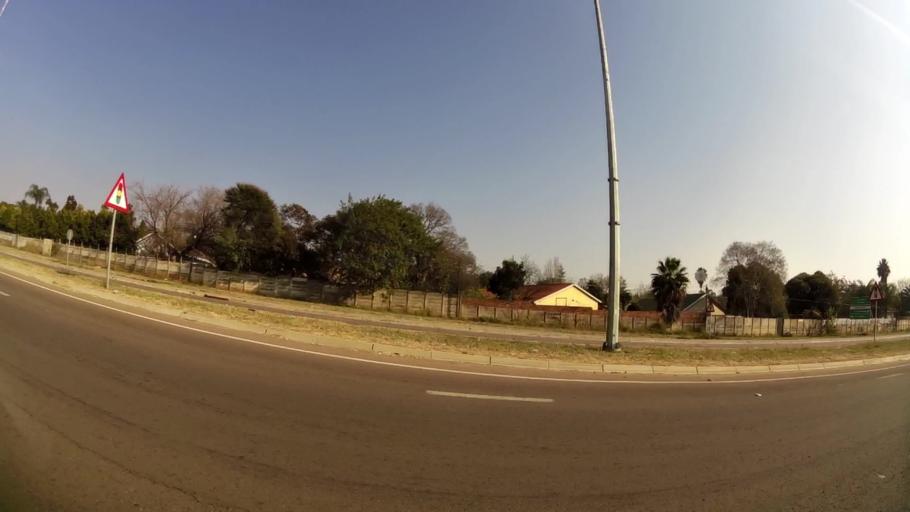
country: ZA
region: Gauteng
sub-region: City of Tshwane Metropolitan Municipality
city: Pretoria
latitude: -25.7396
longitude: 28.3291
